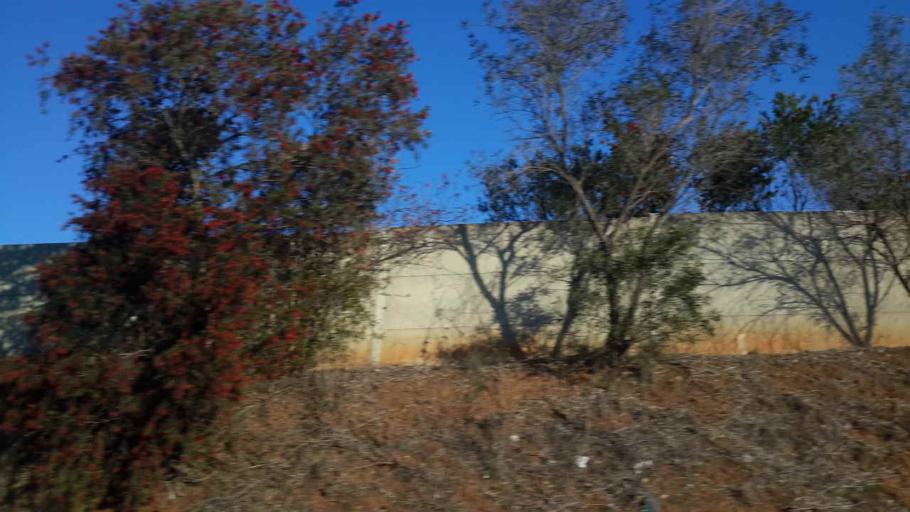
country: AU
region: New South Wales
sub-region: Camden
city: Narellan Vale
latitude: -34.0501
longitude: 150.7418
